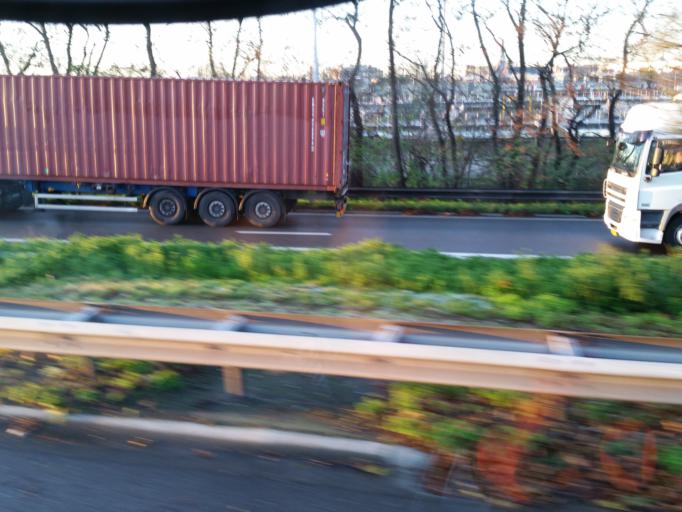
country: BE
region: Flanders
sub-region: Provincie Antwerpen
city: Antwerpen
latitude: 51.2274
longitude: 4.4445
